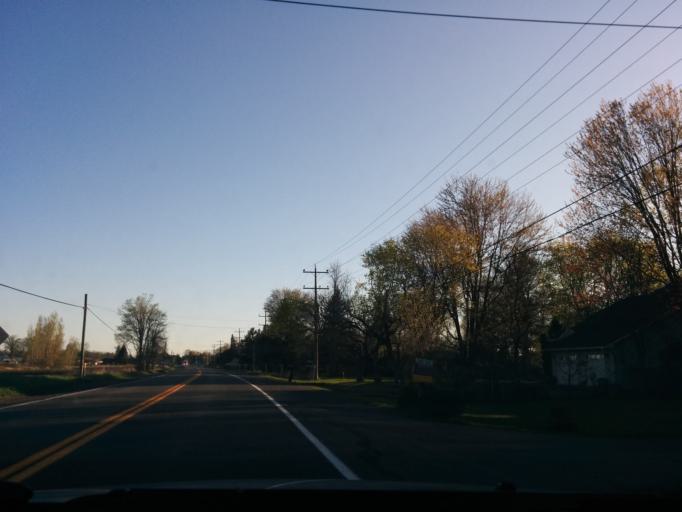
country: CA
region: Ontario
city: Bells Corners
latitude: 45.1666
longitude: -75.6252
